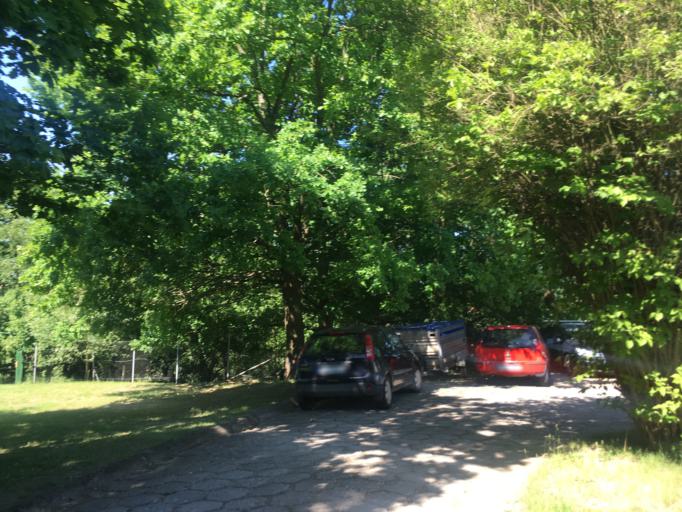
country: PL
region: Warmian-Masurian Voivodeship
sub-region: Olsztyn
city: Kortowo
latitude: 53.7543
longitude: 20.4726
